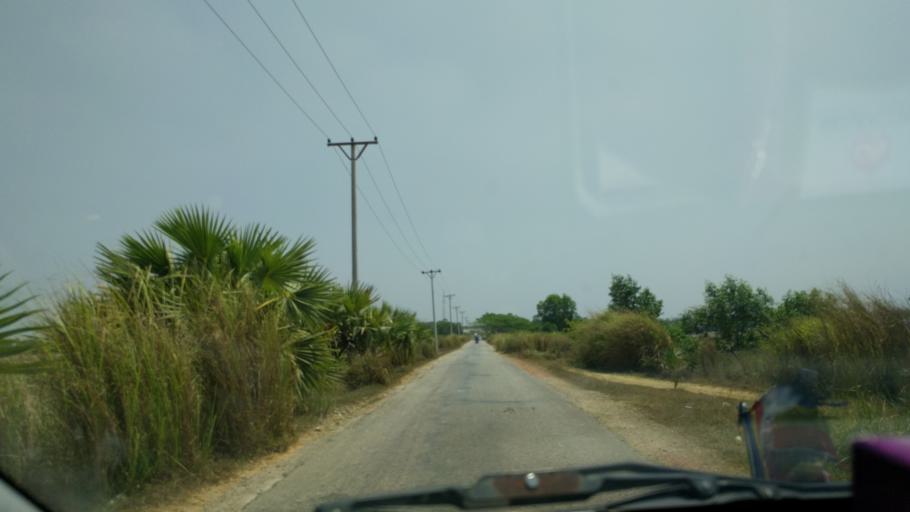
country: MM
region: Mon
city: Martaban
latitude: 16.5863
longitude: 97.6785
